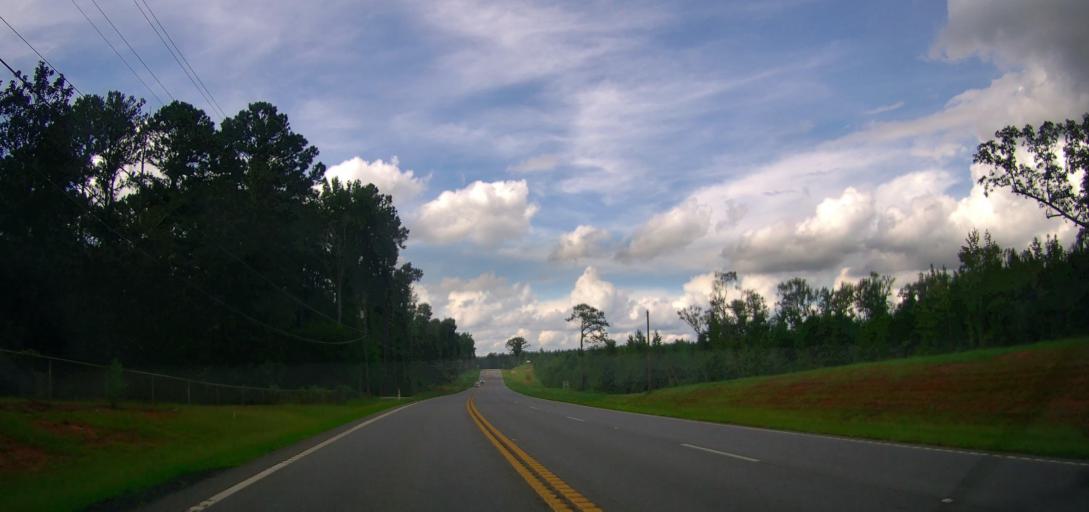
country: US
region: Georgia
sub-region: Harris County
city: Hamilton
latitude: 32.7196
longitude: -84.8735
